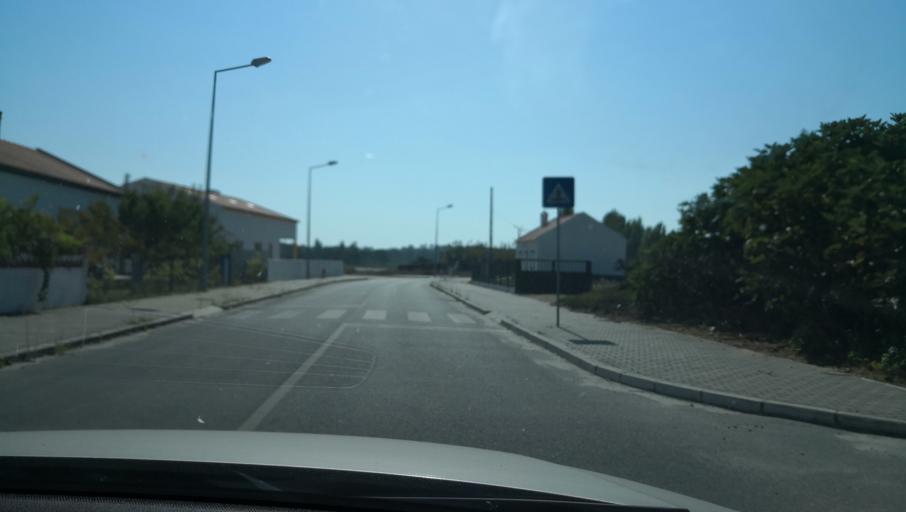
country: PT
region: Setubal
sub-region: Setubal
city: Setubal
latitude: 38.3971
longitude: -8.7727
